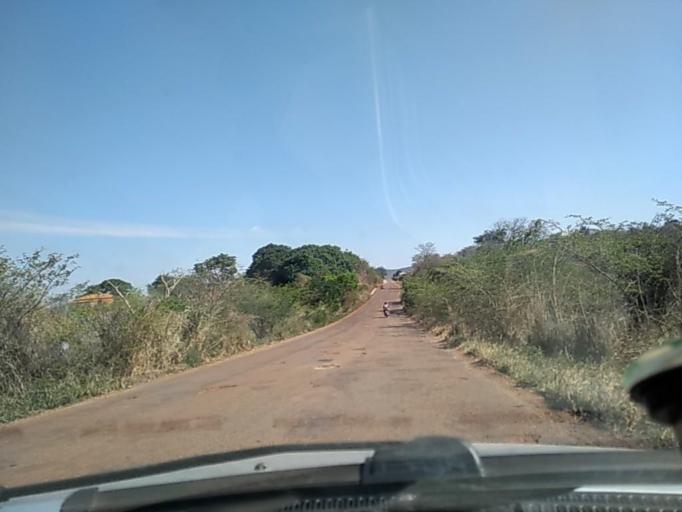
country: BR
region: Bahia
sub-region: Caetite
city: Caetite
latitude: -14.0443
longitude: -42.4857
